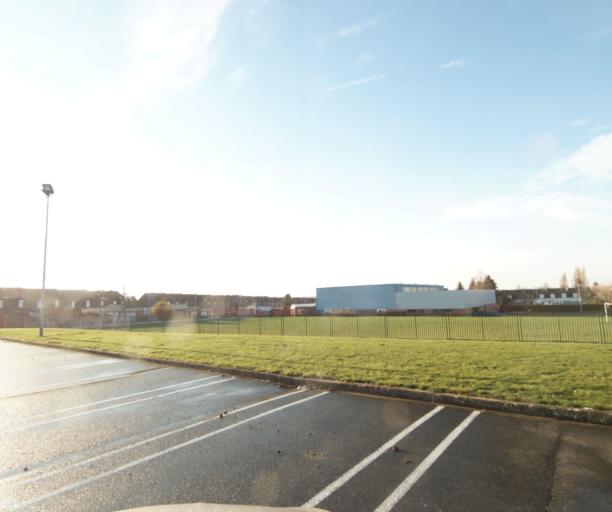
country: FR
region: Nord-Pas-de-Calais
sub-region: Departement du Nord
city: Famars
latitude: 50.3357
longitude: 3.5109
